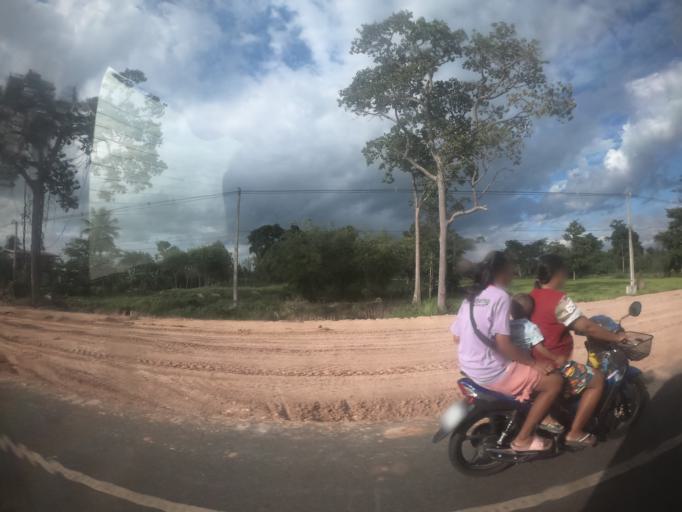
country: TH
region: Surin
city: Kap Choeng
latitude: 14.4869
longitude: 103.5781
